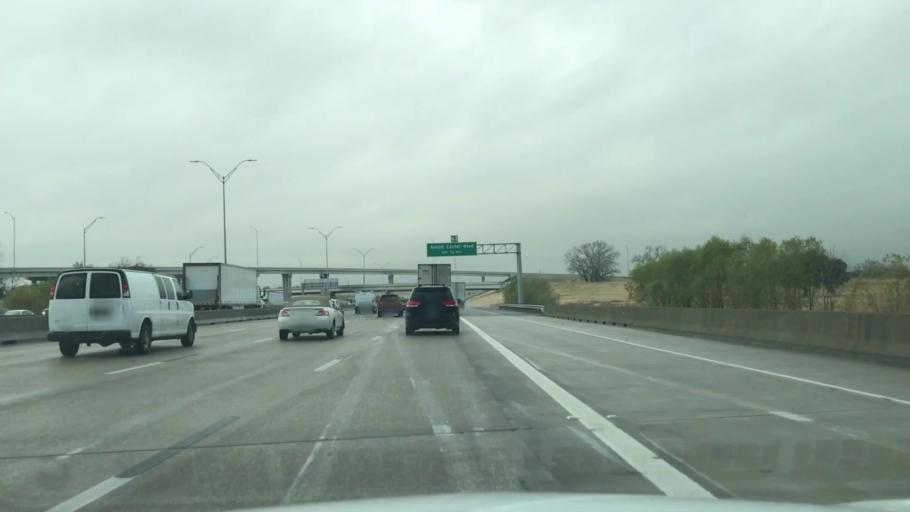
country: US
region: Texas
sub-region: Tarrant County
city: Euless
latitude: 32.8372
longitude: -97.0366
